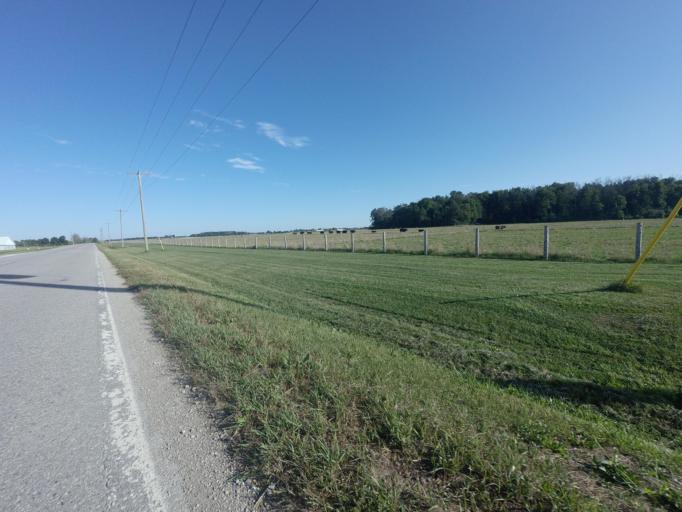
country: CA
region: Ontario
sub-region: Wellington County
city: Guelph
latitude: 43.6457
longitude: -80.4089
